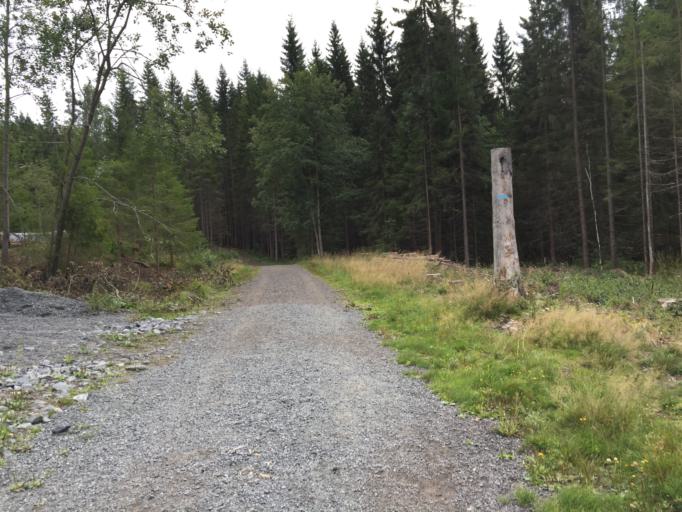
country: NO
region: Akershus
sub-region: Raelingen
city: Fjerdingby
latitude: 59.9171
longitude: 11.0142
